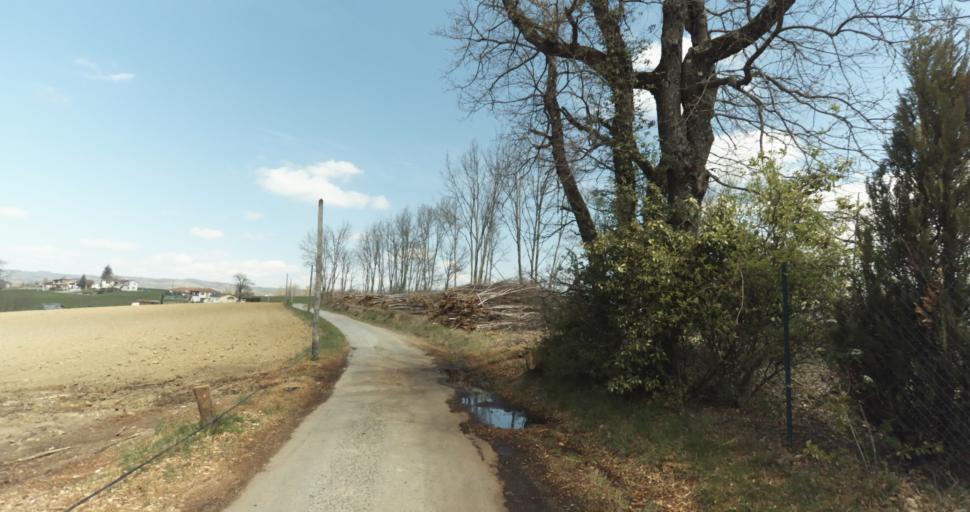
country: FR
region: Rhone-Alpes
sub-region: Departement de l'Isere
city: Saint-Marcellin
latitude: 45.1689
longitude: 5.3087
